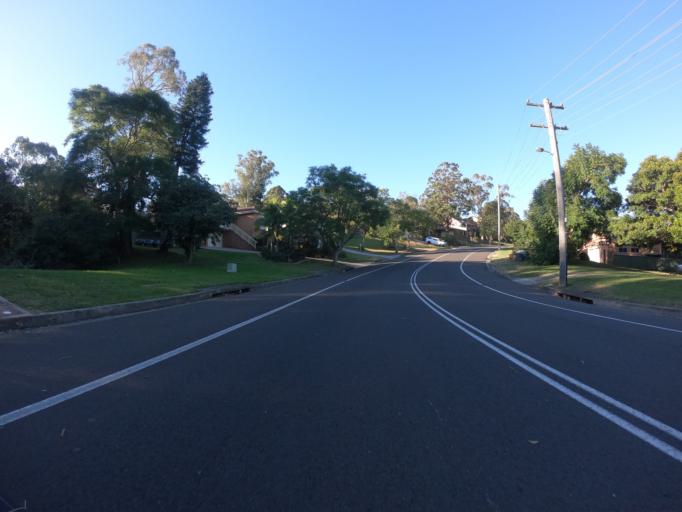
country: AU
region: New South Wales
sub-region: Wollongong
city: Cordeaux Heights
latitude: -34.4331
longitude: 150.8466
